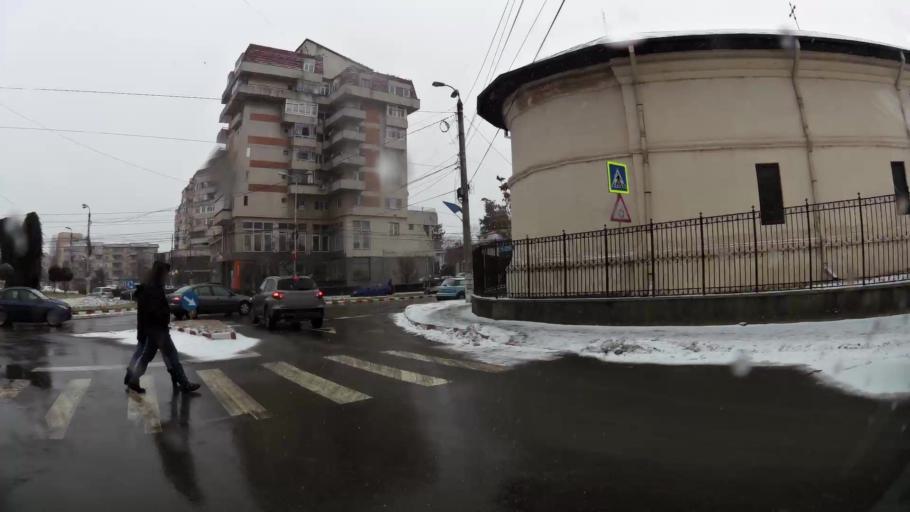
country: RO
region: Dambovita
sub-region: Municipiul Targoviste
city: Targoviste
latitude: 44.9245
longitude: 25.4570
